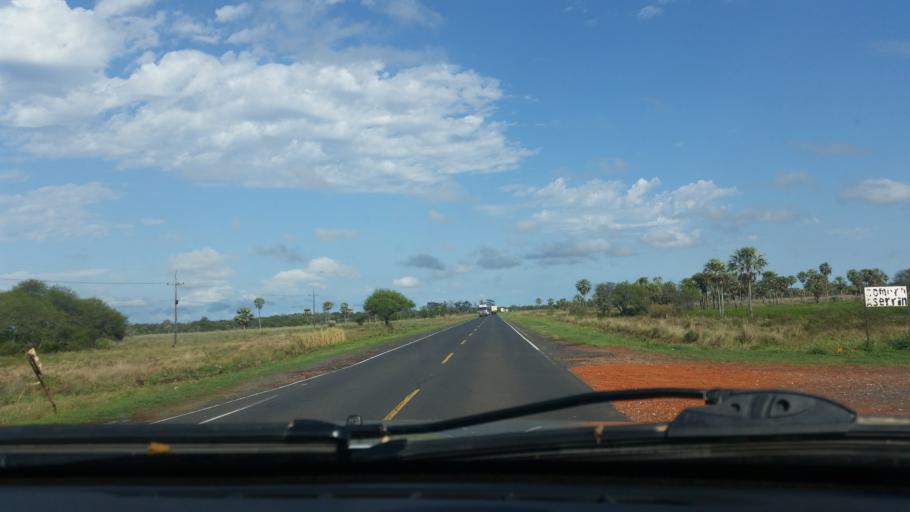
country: PY
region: Presidente Hayes
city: Benjamin Aceval
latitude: -24.9208
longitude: -57.5951
